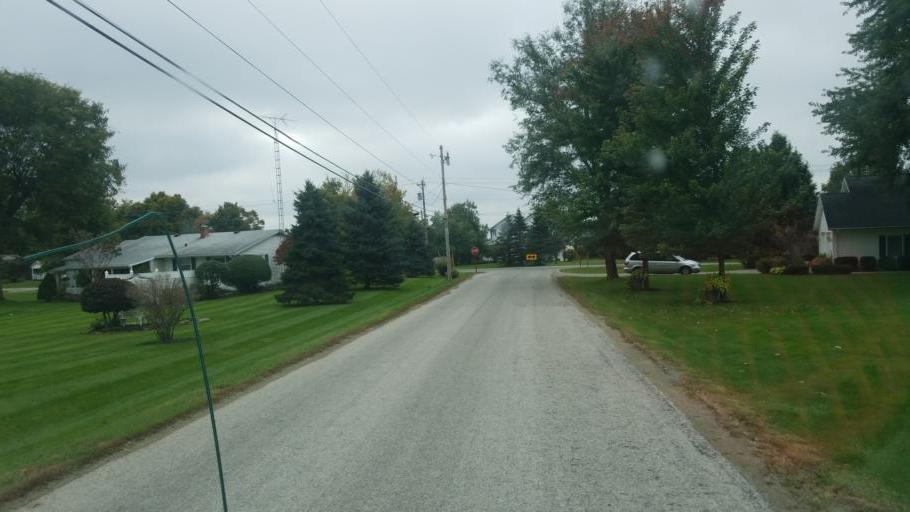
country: US
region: Ohio
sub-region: Richland County
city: Lexington
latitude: 40.6515
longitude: -82.6232
